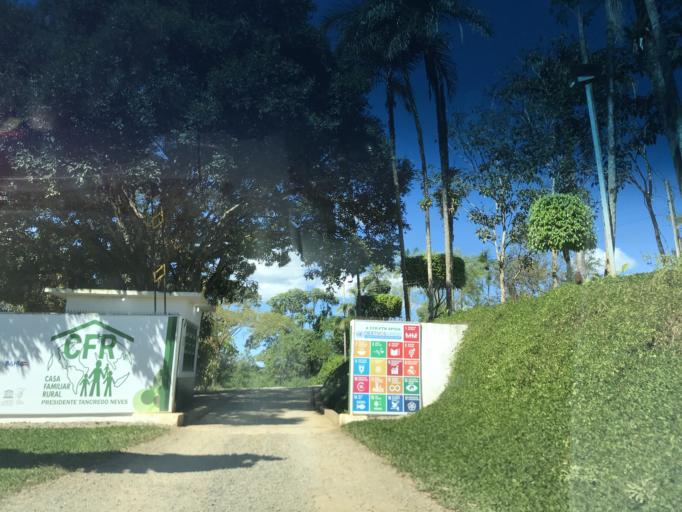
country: BR
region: Bahia
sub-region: Mutuipe
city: Mutuipe
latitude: -13.3720
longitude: -39.3710
